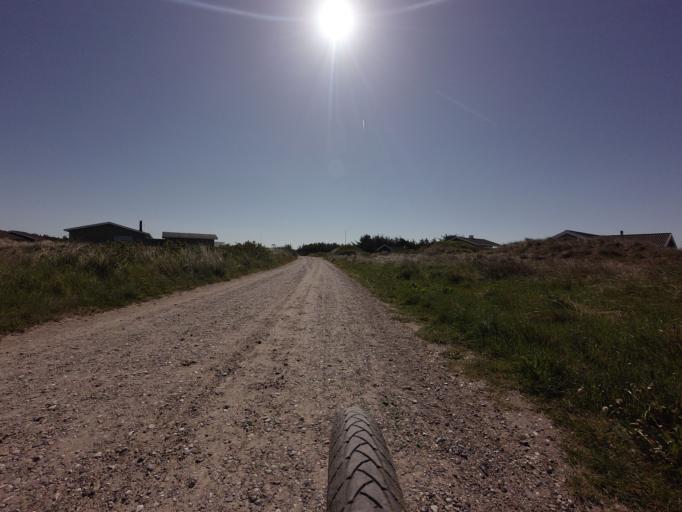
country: DK
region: North Denmark
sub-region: Jammerbugt Kommune
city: Pandrup
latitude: 57.3354
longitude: 9.6768
